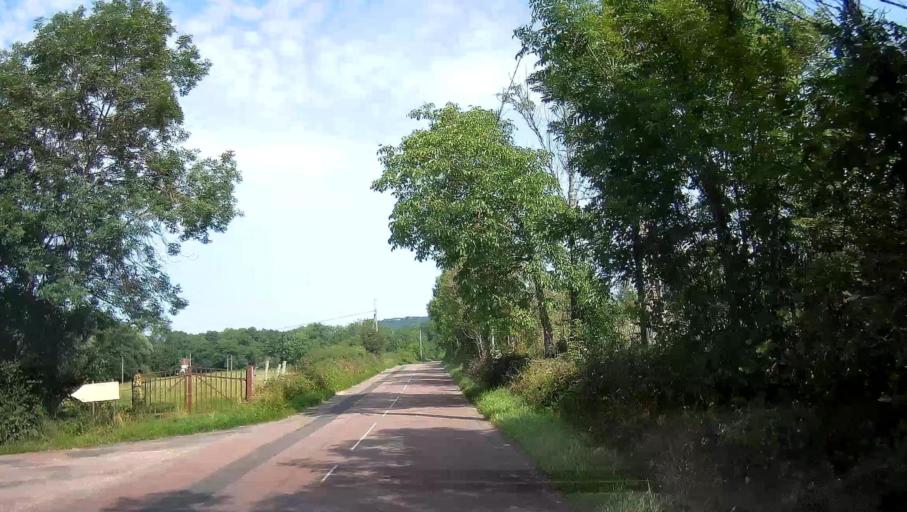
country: FR
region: Bourgogne
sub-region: Departement de la Cote-d'Or
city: Nolay
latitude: 46.9410
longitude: 4.6290
